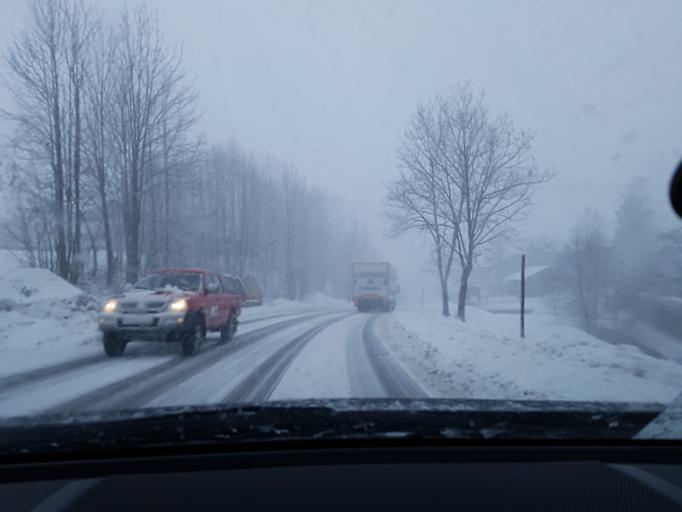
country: AT
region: Salzburg
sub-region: Politischer Bezirk Hallein
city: Abtenau
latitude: 47.5694
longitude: 13.3345
